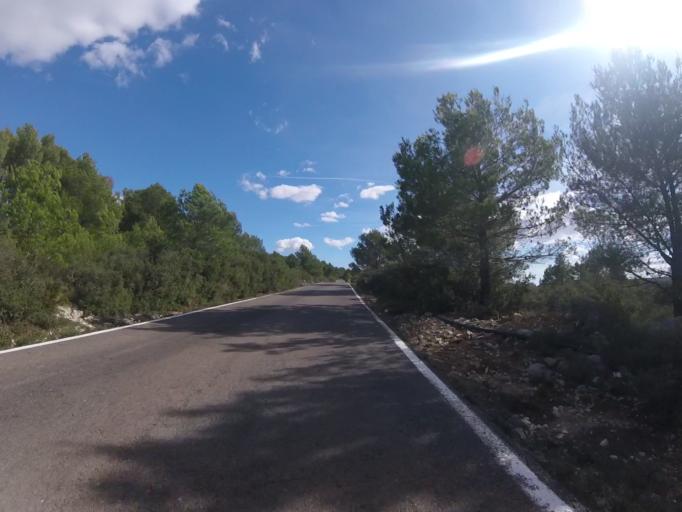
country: ES
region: Valencia
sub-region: Provincia de Castello
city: Albocasser
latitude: 40.4061
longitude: 0.0759
